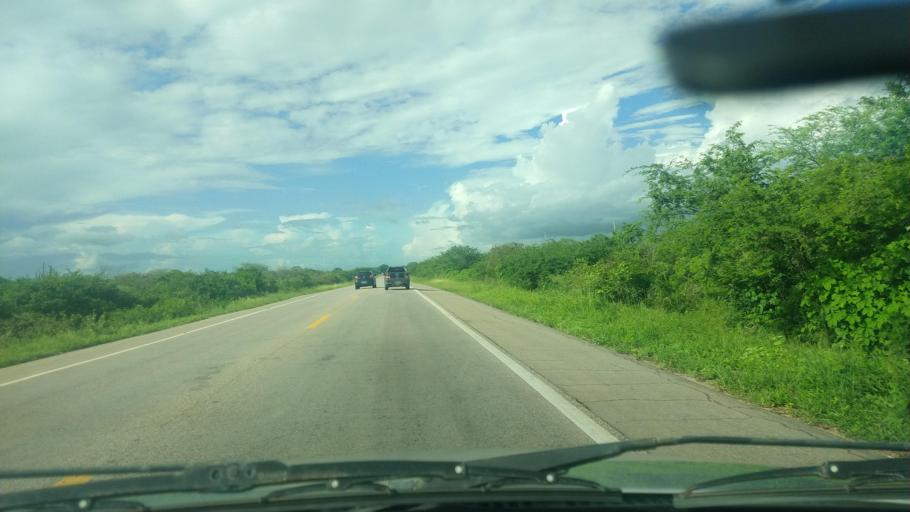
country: BR
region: Rio Grande do Norte
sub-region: Tangara
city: Tangara
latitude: -6.1691
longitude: -35.7607
